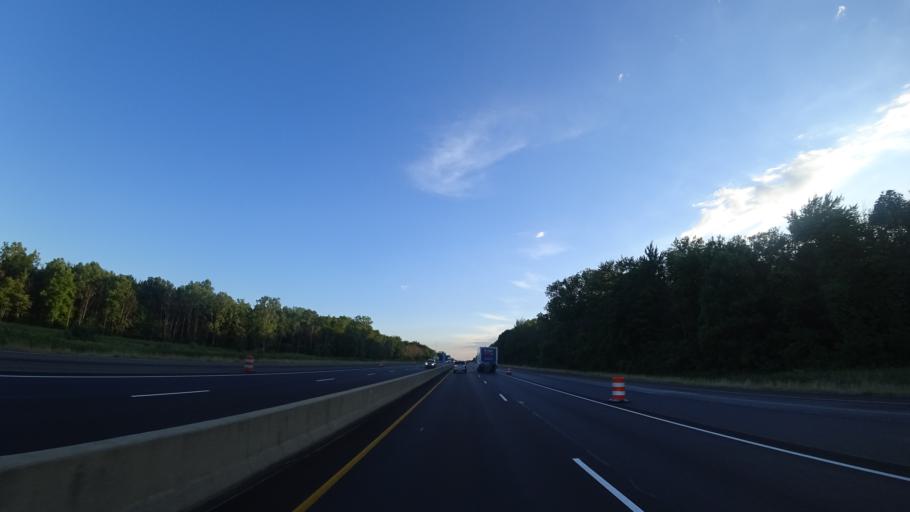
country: US
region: Michigan
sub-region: Berrien County
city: New Buffalo
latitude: 41.7511
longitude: -86.7652
